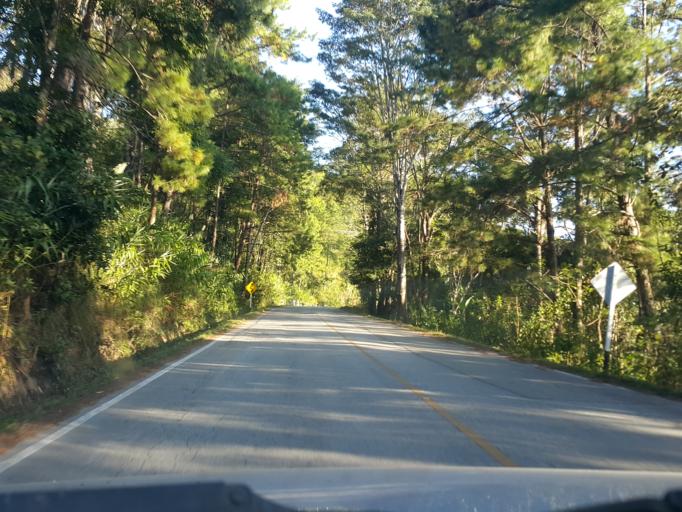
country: TH
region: Mae Hong Son
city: Mae Hi
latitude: 19.2680
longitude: 98.5815
